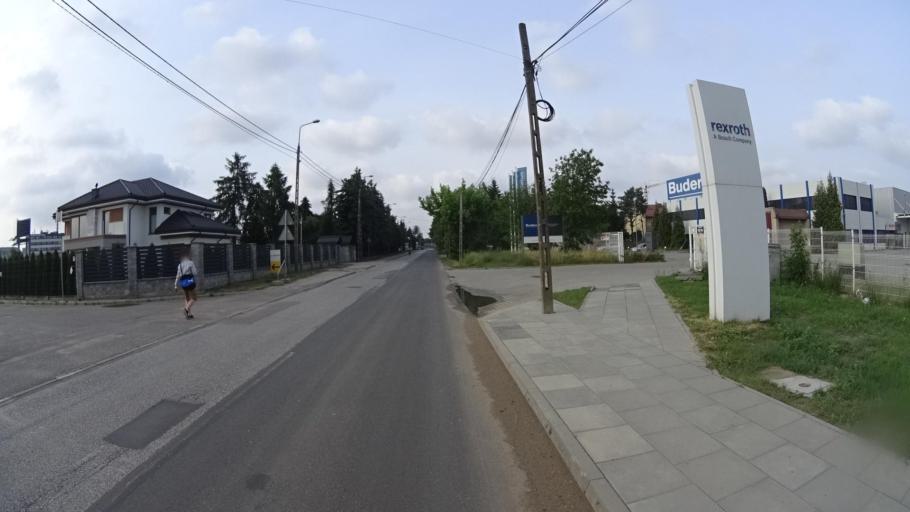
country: PL
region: Masovian Voivodeship
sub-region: Warszawa
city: Wlochy
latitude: 52.1912
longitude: 20.9278
